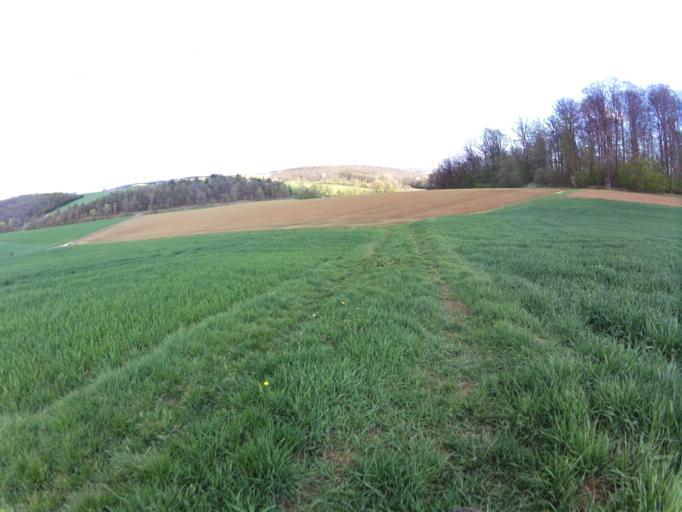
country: DE
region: Bavaria
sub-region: Regierungsbezirk Unterfranken
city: Waldbrunn
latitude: 49.7821
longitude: 9.7973
